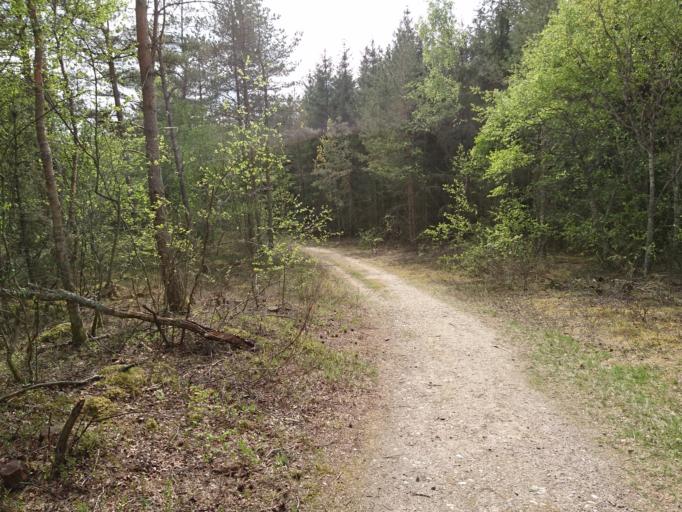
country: DK
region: North Denmark
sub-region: Frederikshavn Kommune
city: Skagen
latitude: 57.7117
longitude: 10.5197
